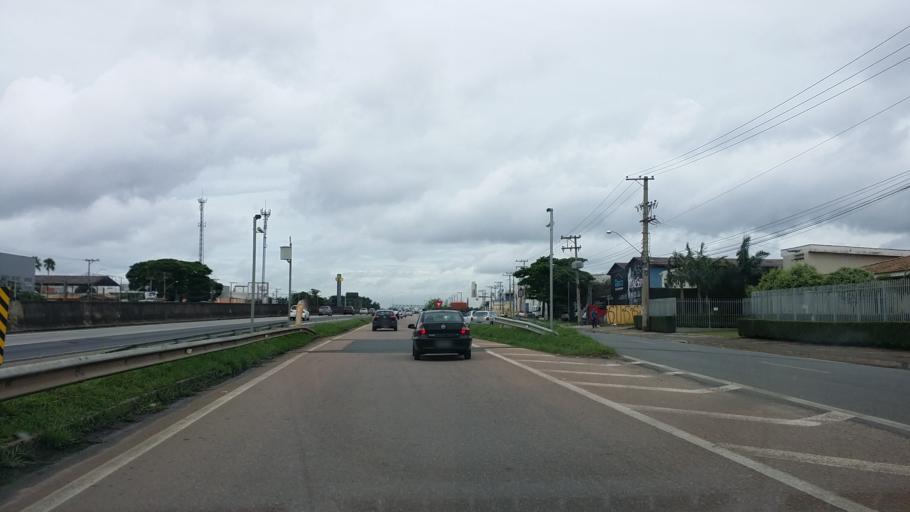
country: BR
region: Sao Paulo
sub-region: Indaiatuba
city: Indaiatuba
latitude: -23.1220
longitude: -47.2227
